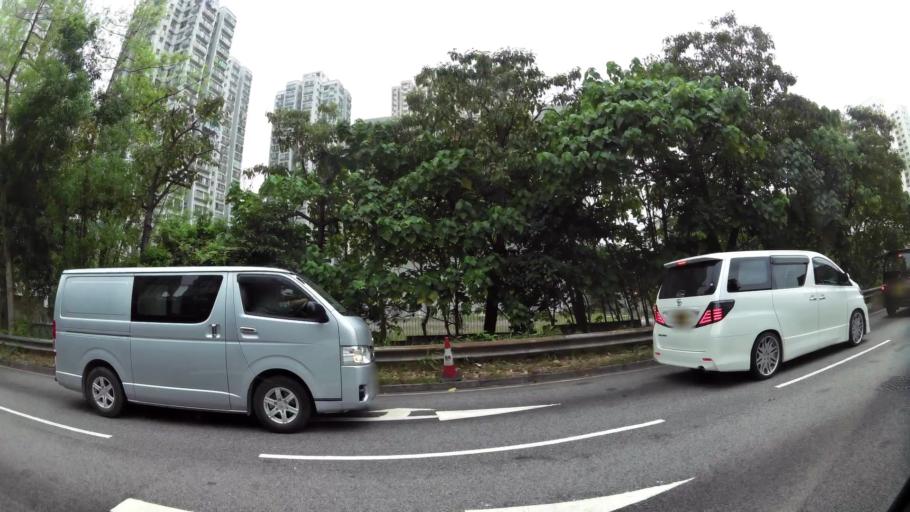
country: HK
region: Tai Po
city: Tai Po
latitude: 22.4538
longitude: 114.1723
